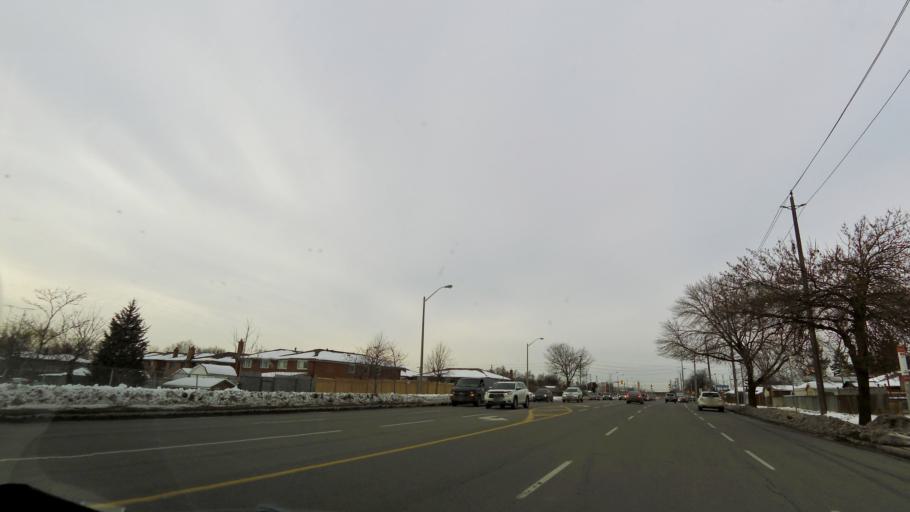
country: CA
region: Ontario
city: Concord
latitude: 43.7628
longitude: -79.5736
